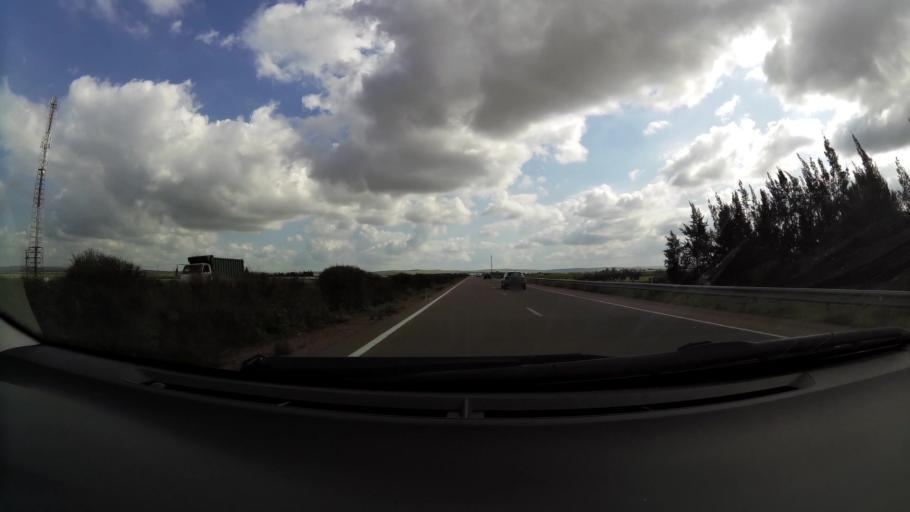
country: MA
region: Chaouia-Ouardigha
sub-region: Settat Province
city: Berrechid
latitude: 33.1437
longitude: -7.5746
